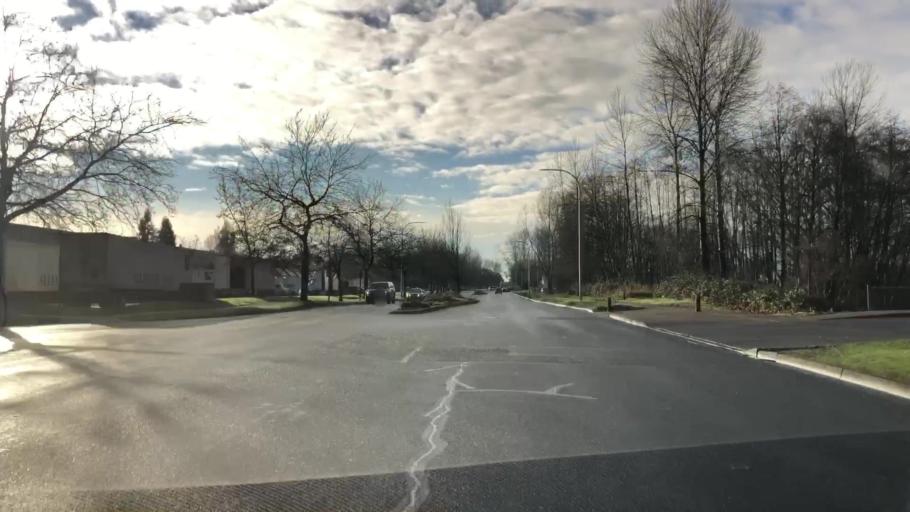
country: US
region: Washington
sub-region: King County
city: Tukwila
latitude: 47.4439
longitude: -122.2329
